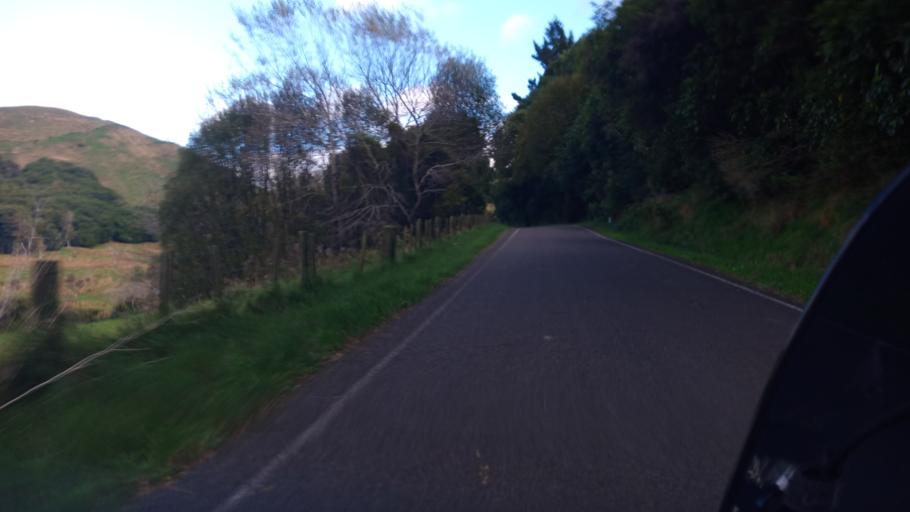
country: NZ
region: Gisborne
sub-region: Gisborne District
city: Gisborne
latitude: -38.5333
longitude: 177.5548
